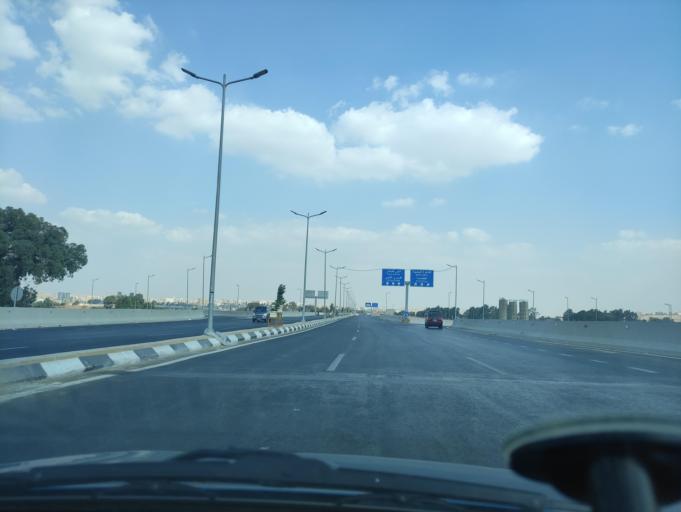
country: EG
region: Muhafazat al Qahirah
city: Cairo
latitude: 30.0399
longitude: 31.3041
